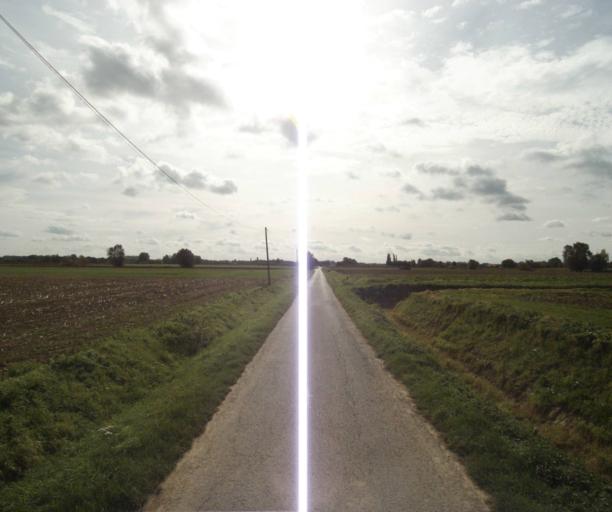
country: FR
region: Nord-Pas-de-Calais
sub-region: Departement du Nord
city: Bois-Grenier
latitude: 50.6302
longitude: 2.8717
